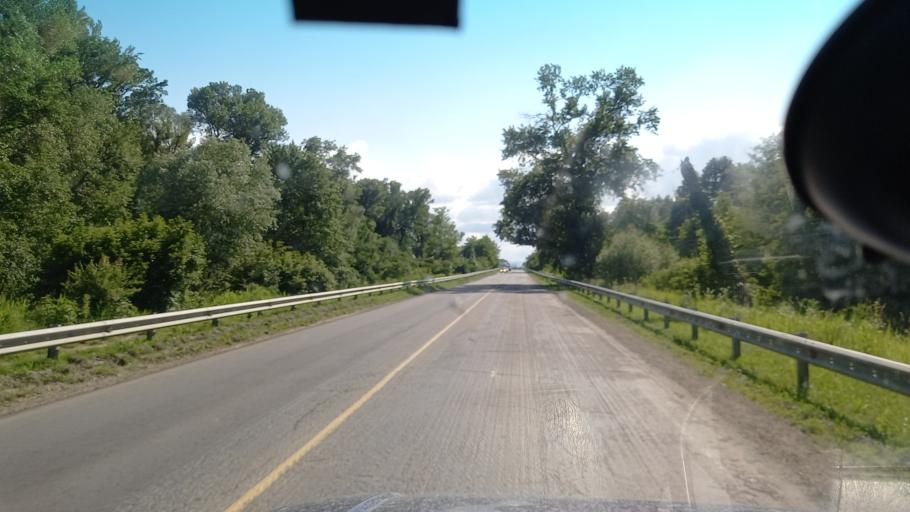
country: RU
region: Krasnodarskiy
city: Mostovskoy
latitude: 44.4026
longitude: 40.8279
